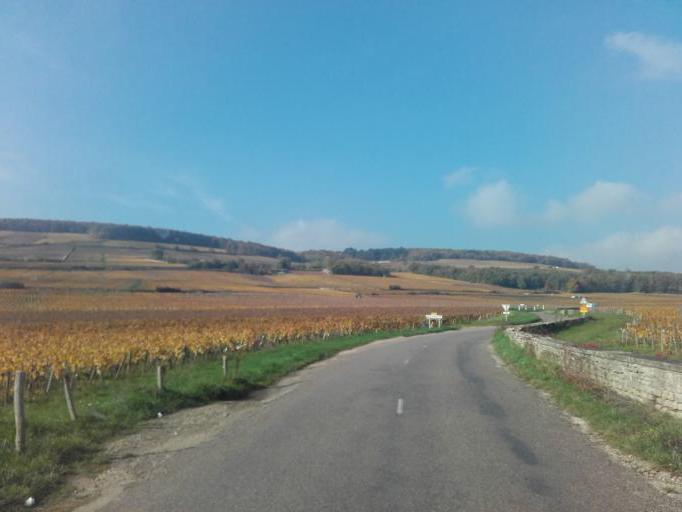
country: FR
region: Bourgogne
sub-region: Departement de la Cote-d'Or
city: Beaune
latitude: 47.0753
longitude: 4.8803
